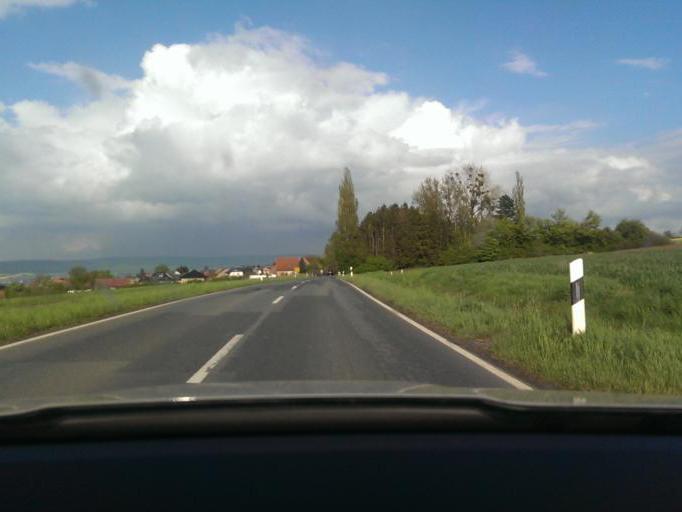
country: DE
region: Lower Saxony
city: Rehren
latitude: 52.2371
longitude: 9.2877
